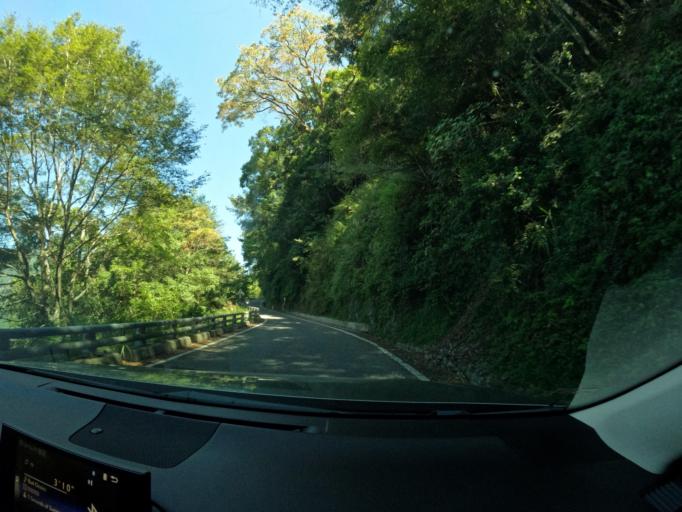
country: TW
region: Taiwan
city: Yujing
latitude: 23.2828
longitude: 120.8771
